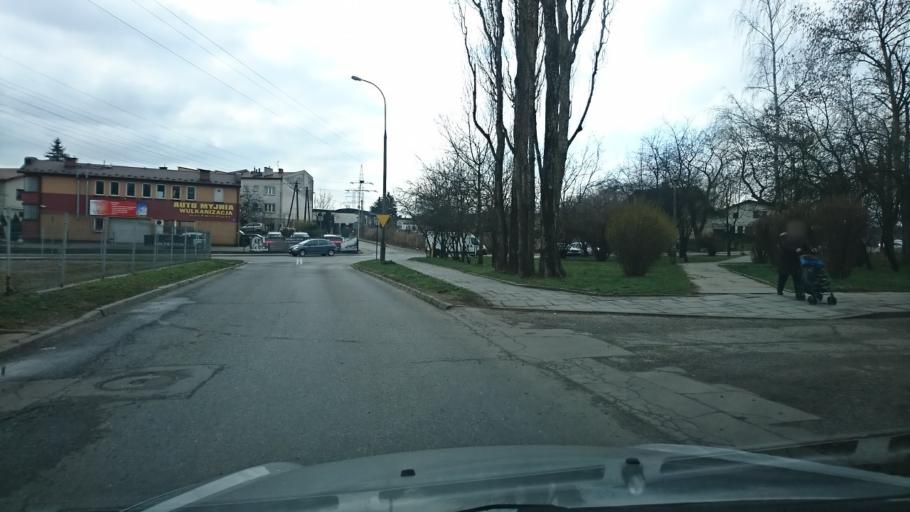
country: PL
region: Lesser Poland Voivodeship
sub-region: Powiat wielicki
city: Czarnochowice
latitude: 50.0117
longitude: 20.0237
